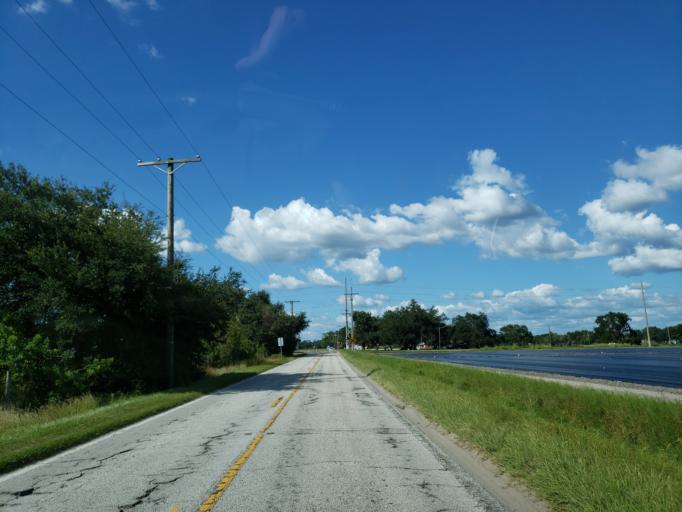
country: US
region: Florida
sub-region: Hillsborough County
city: Dover
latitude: 27.9655
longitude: -82.2031
